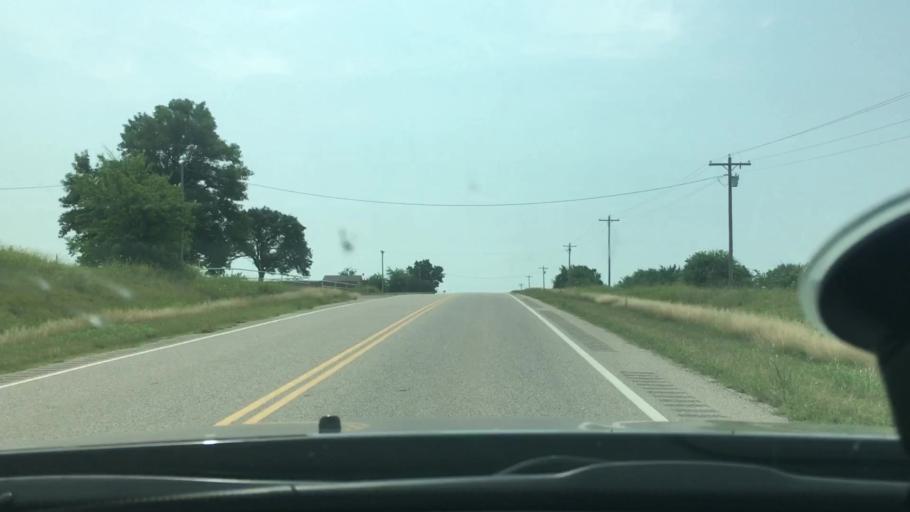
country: US
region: Oklahoma
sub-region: Marshall County
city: Kingston
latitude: 34.0344
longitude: -96.7611
